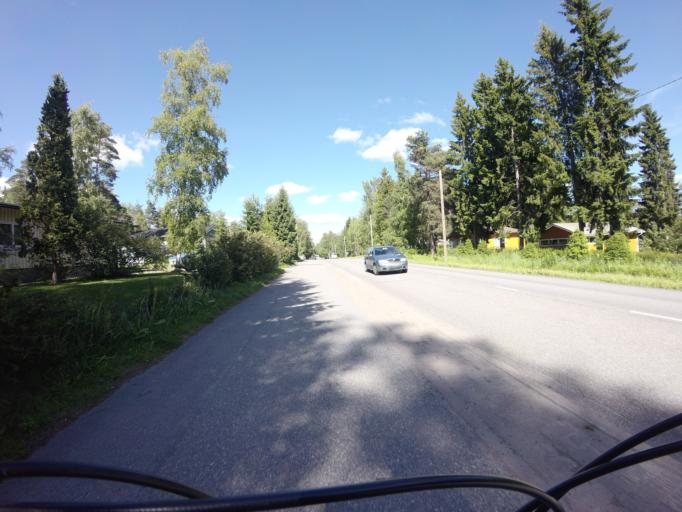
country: FI
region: Varsinais-Suomi
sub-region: Turku
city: Vahto
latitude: 60.5306
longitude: 22.2995
